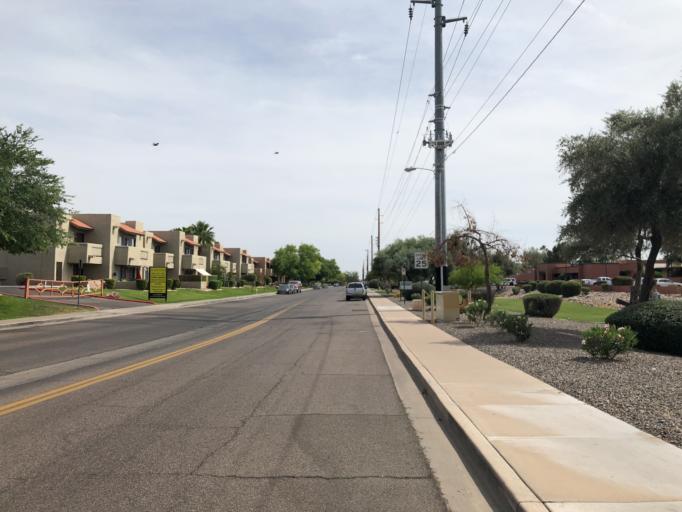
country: US
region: Arizona
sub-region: Maricopa County
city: Tempe
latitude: 33.4584
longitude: -111.9007
